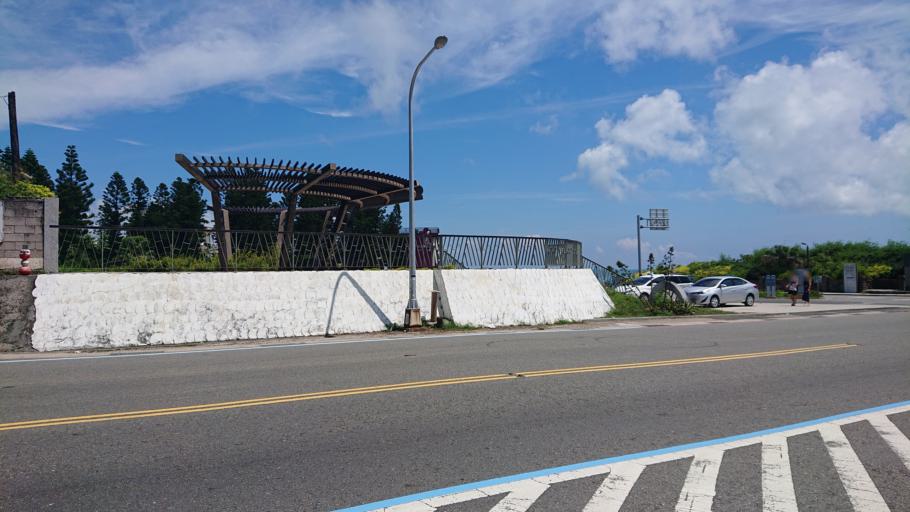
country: TW
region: Taiwan
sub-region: Penghu
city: Ma-kung
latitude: 23.6584
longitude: 119.5550
